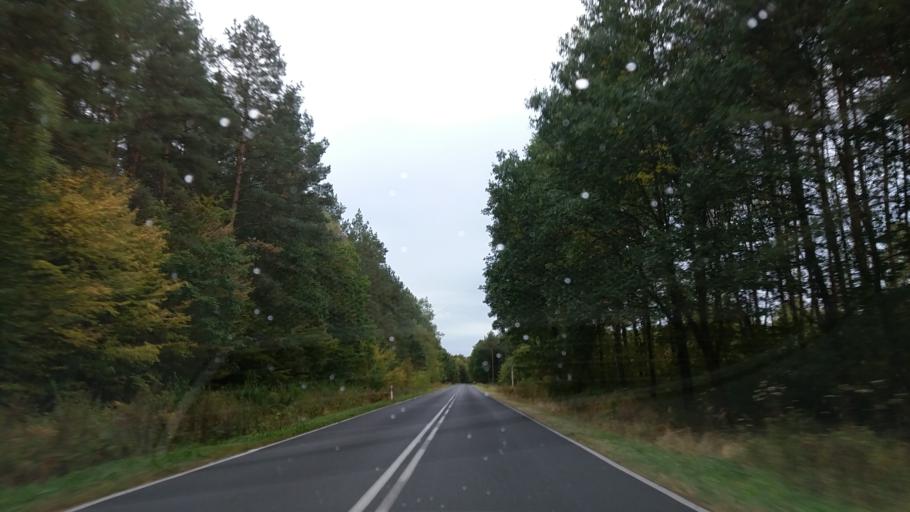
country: PL
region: West Pomeranian Voivodeship
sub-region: Powiat mysliborski
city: Barlinek
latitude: 52.9036
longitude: 15.1920
